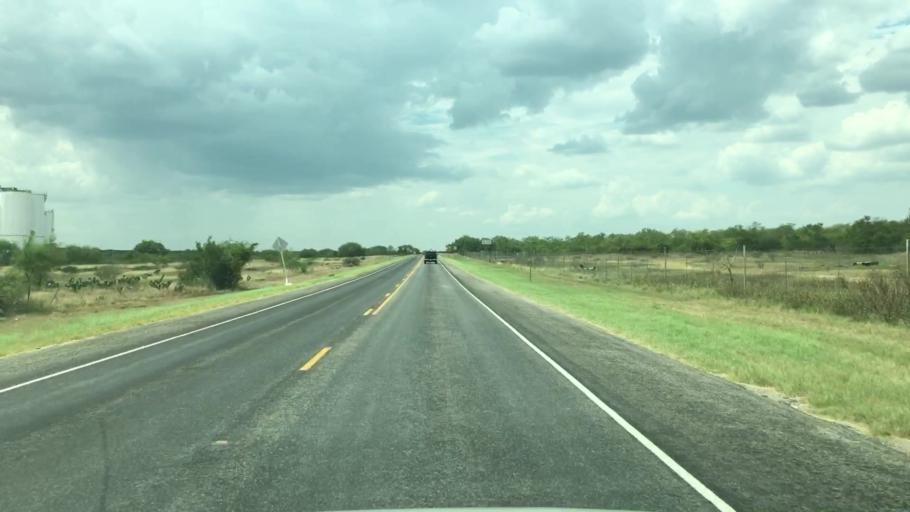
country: US
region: Texas
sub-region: Live Oak County
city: Three Rivers
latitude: 28.6371
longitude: -98.2766
